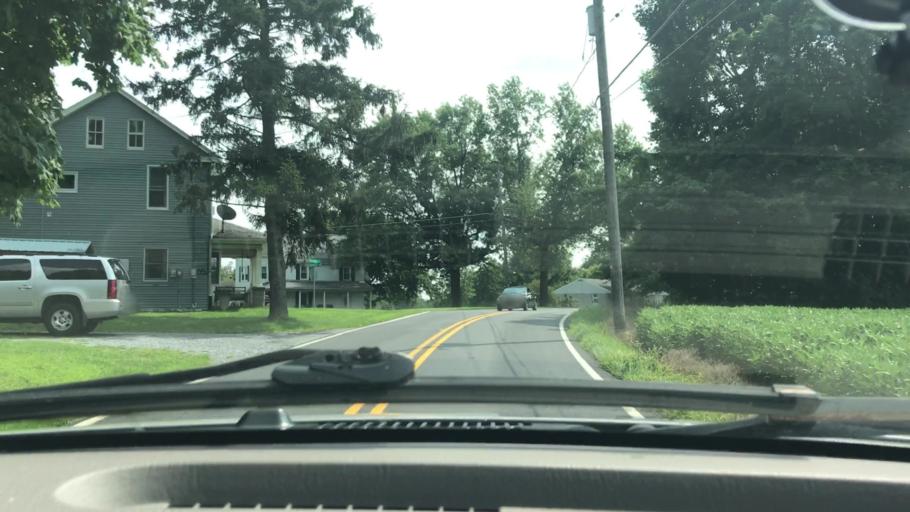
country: US
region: Pennsylvania
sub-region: Lancaster County
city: Rheems
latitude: 40.1417
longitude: -76.5732
